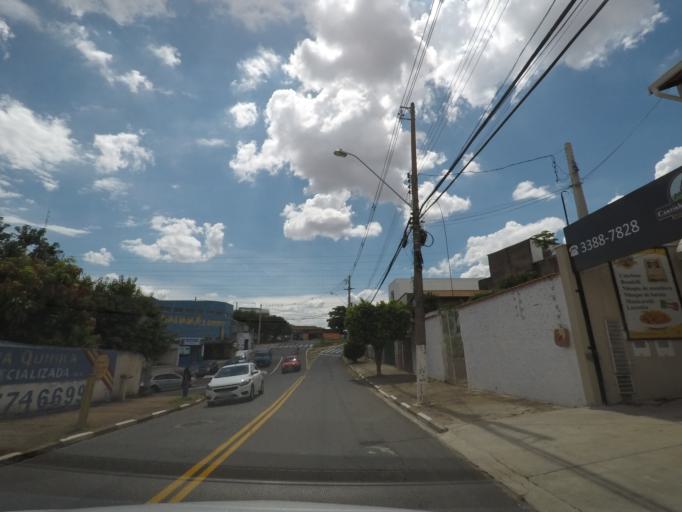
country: BR
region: Sao Paulo
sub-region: Campinas
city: Campinas
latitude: -22.9261
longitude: -47.0268
